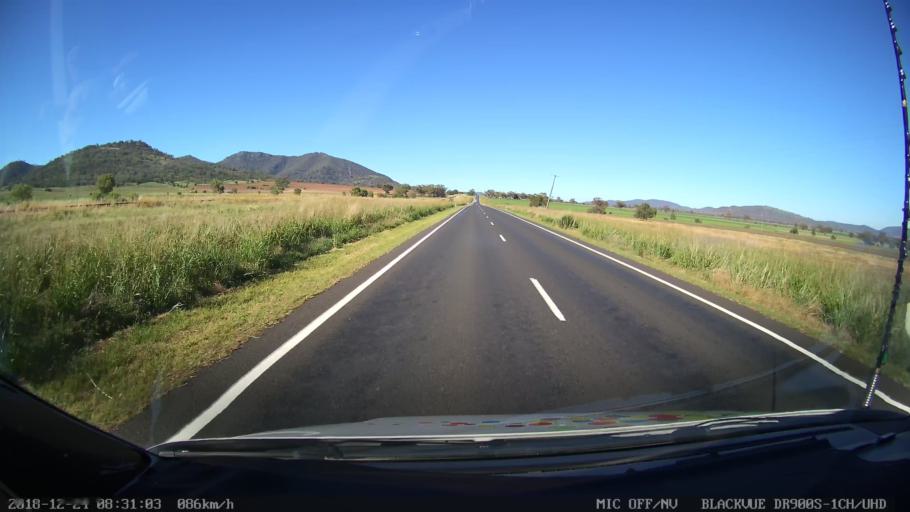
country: AU
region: New South Wales
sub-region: Tamworth Municipality
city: Phillip
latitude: -31.2712
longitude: 150.7167
